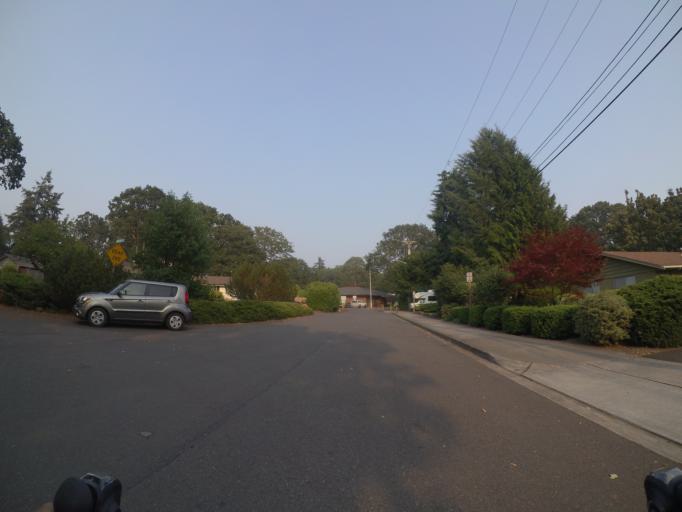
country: US
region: Washington
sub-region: Pierce County
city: Lakewood
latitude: 47.1795
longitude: -122.5145
